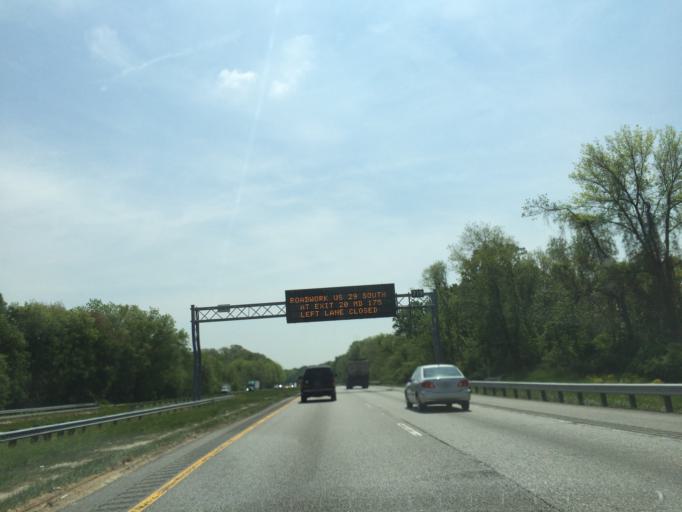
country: US
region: Maryland
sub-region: Howard County
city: Columbia
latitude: 39.3011
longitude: -76.8709
